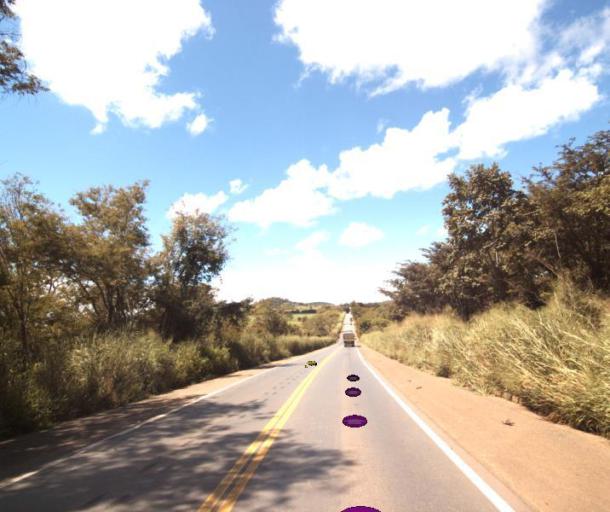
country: BR
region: Goias
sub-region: Pirenopolis
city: Pirenopolis
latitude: -16.0360
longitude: -49.0834
